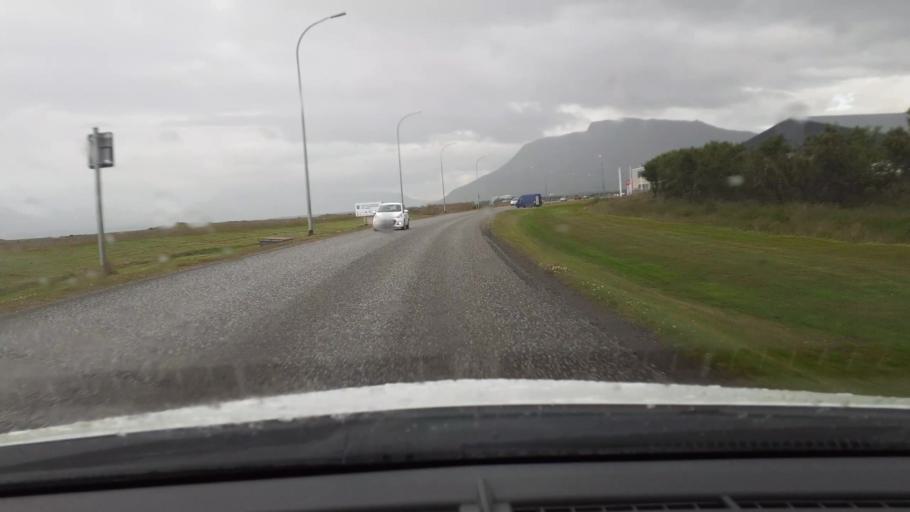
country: IS
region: West
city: Akranes
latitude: 64.3265
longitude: -22.0643
